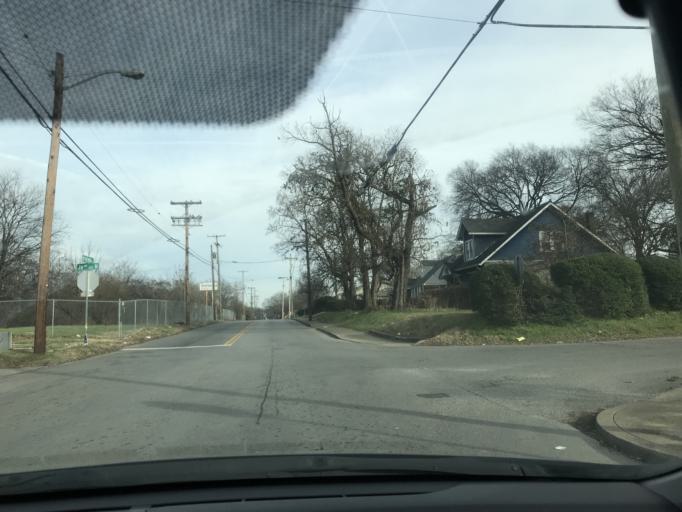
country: US
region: Tennessee
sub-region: Davidson County
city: Nashville
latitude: 36.1701
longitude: -86.8173
